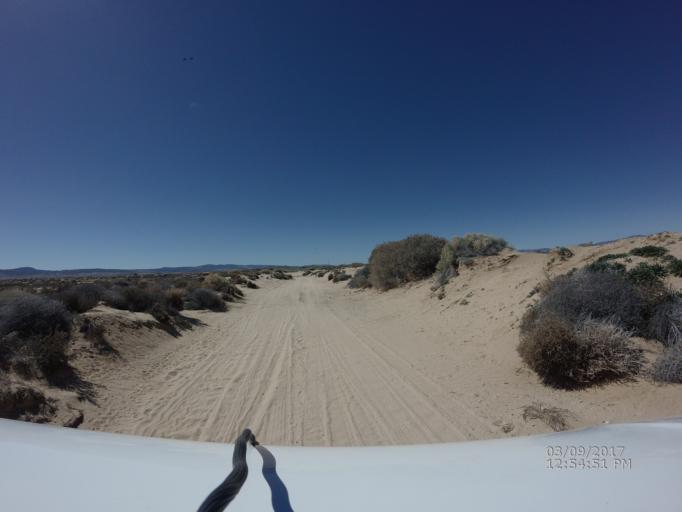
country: US
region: California
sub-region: Los Angeles County
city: Leona Valley
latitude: 34.7474
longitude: -118.2990
